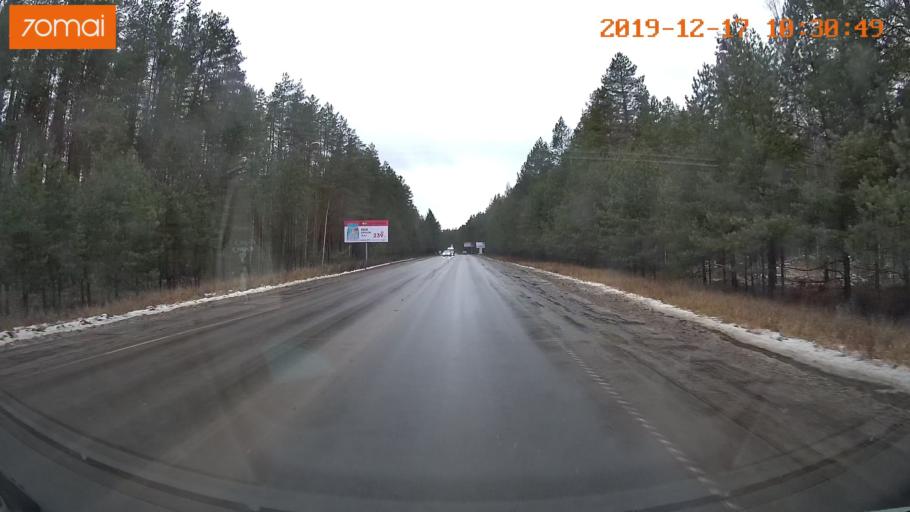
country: RU
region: Vladimir
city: Gus'-Khrustal'nyy
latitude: 55.6398
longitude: 40.7040
